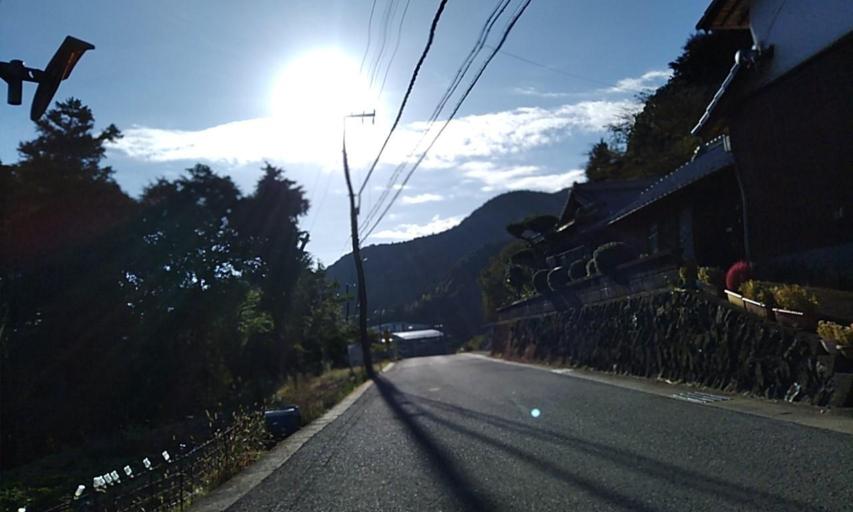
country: JP
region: Wakayama
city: Iwade
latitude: 34.1540
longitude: 135.3081
